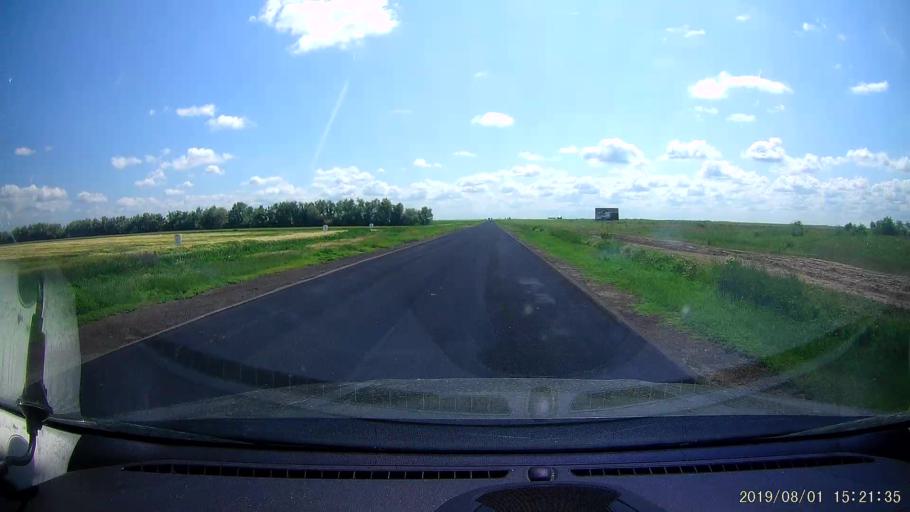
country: RO
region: Braila
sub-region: Comuna Tufesti
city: Tufesti
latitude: 45.0676
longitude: 27.7933
